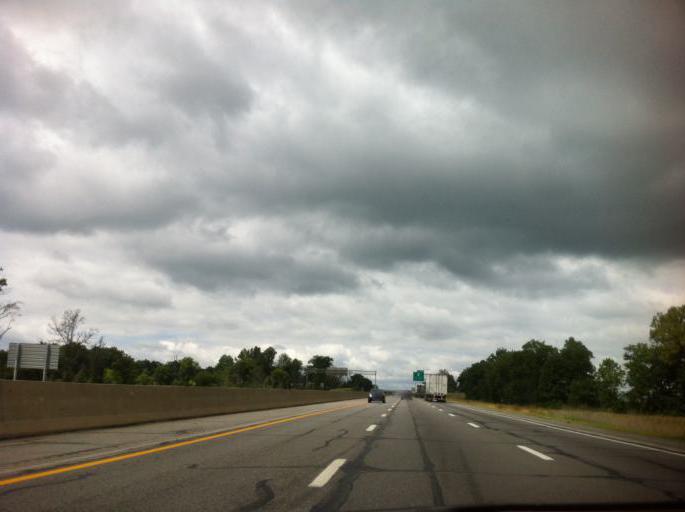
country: US
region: Ohio
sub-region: Portage County
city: Mantua
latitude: 41.2444
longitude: -81.2219
